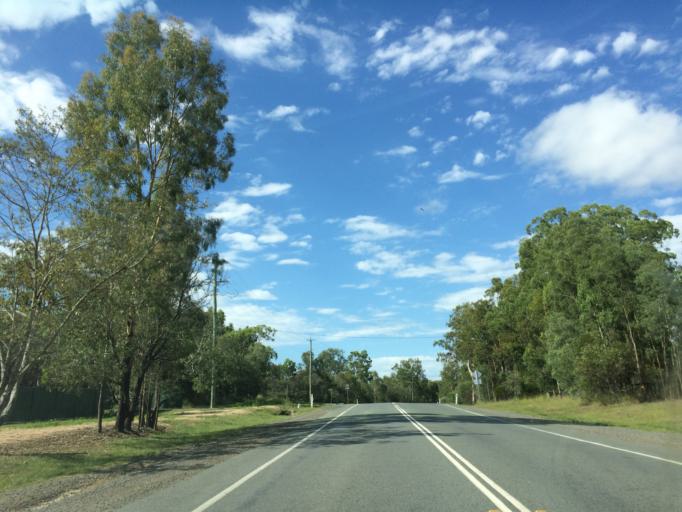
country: AU
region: Queensland
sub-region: Logan
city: North Maclean
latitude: -27.8064
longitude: 152.9821
